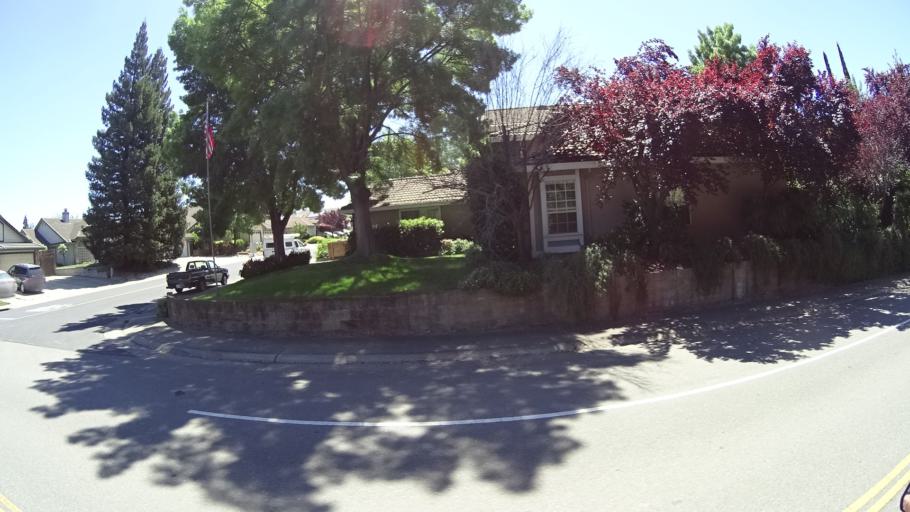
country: US
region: California
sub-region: Placer County
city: Rocklin
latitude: 38.7833
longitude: -121.2068
